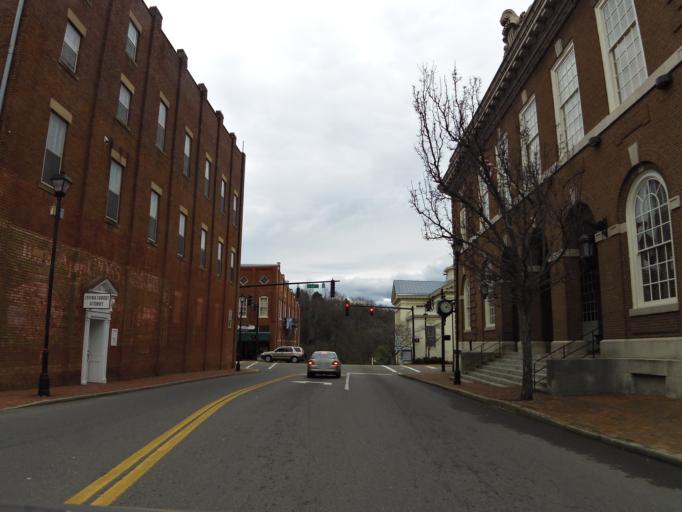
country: US
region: Tennessee
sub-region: Greene County
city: Greeneville
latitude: 36.1624
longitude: -82.8319
